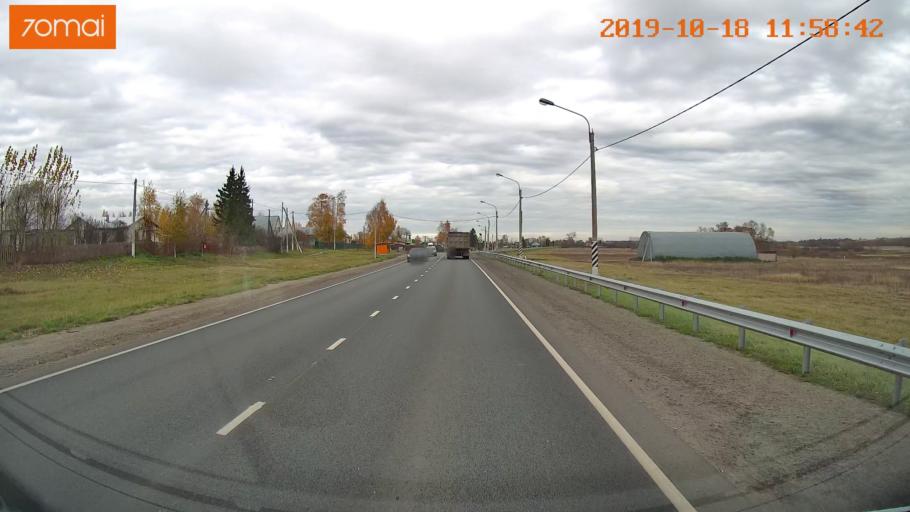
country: RU
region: Rjazan
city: Zakharovo
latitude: 54.2745
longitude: 39.1691
